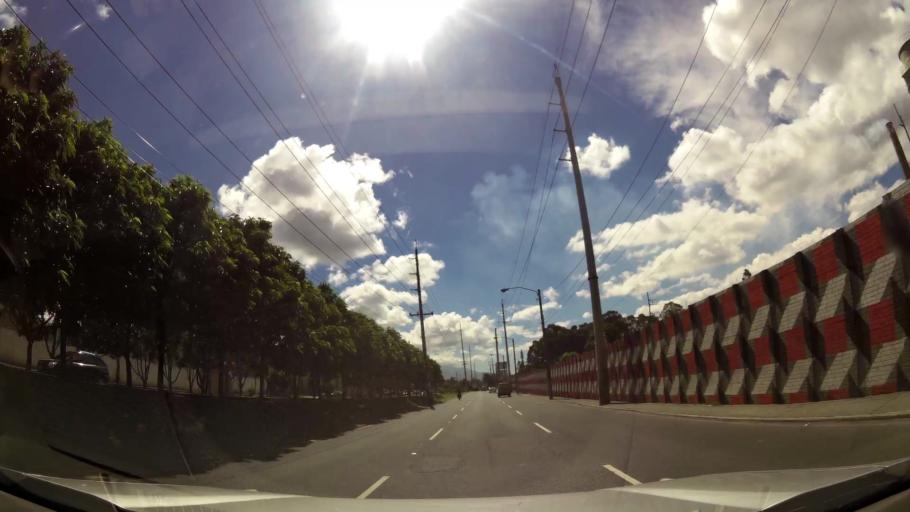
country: GT
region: Guatemala
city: Santa Catarina Pinula
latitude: 14.5638
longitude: -90.5457
